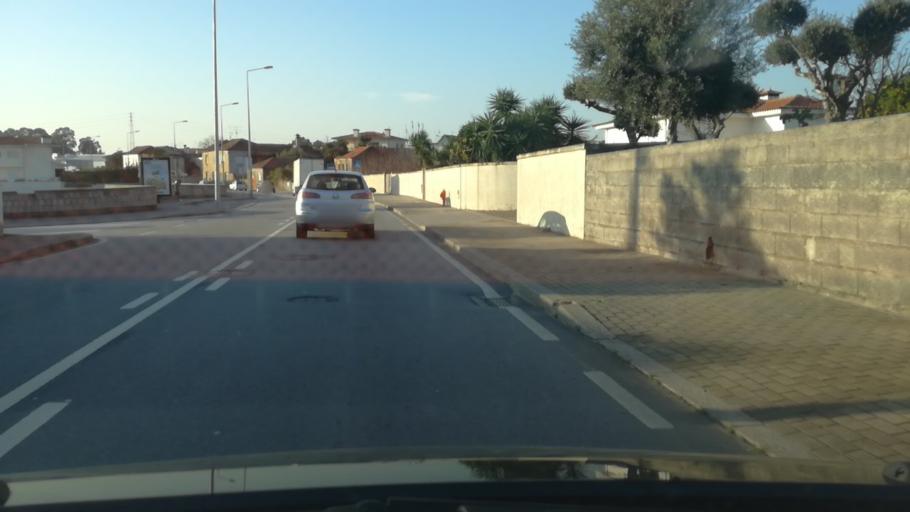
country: PT
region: Porto
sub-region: Trofa
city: Bougado
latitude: 41.3400
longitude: -8.5394
